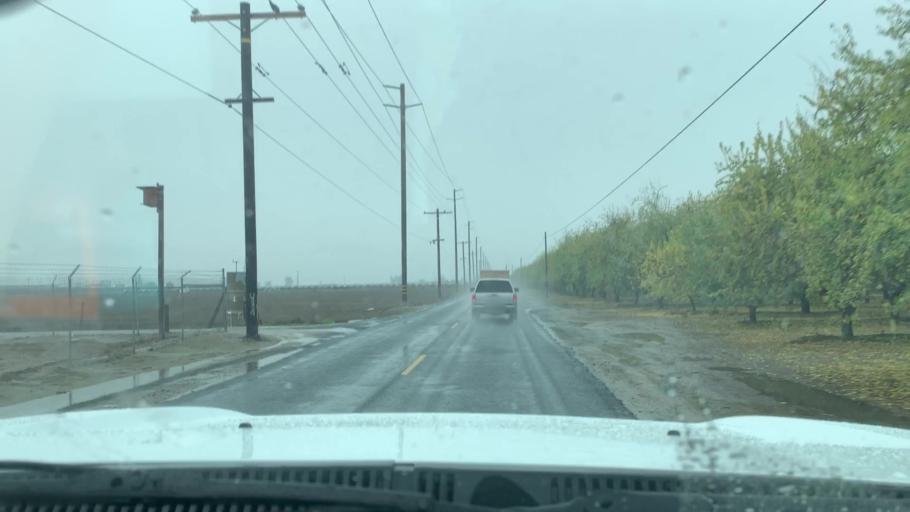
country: US
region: California
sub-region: Tulare County
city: Earlimart
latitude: 35.8339
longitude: -119.2367
